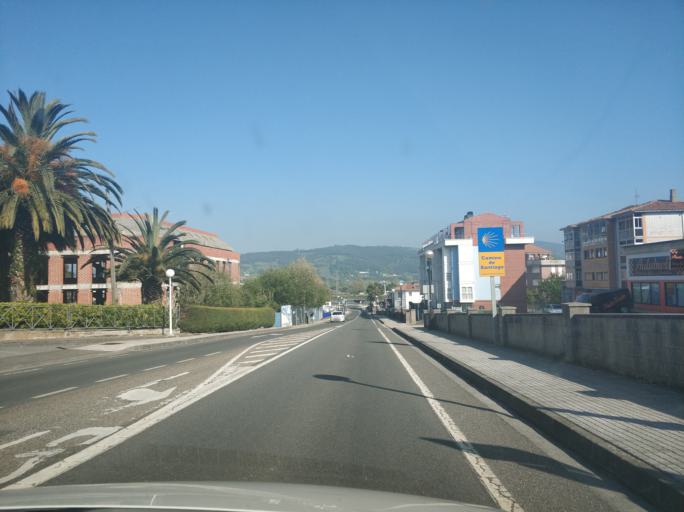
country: ES
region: Cantabria
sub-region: Provincia de Cantabria
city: Colindres
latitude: 43.3936
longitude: -3.4702
